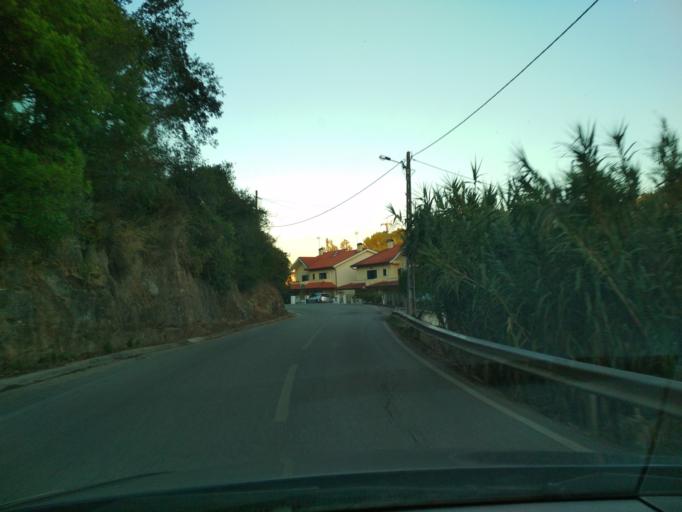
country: PT
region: Coimbra
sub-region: Condeixa-A-Nova
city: Condeixa-a-Nova
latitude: 40.1676
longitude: -8.4736
